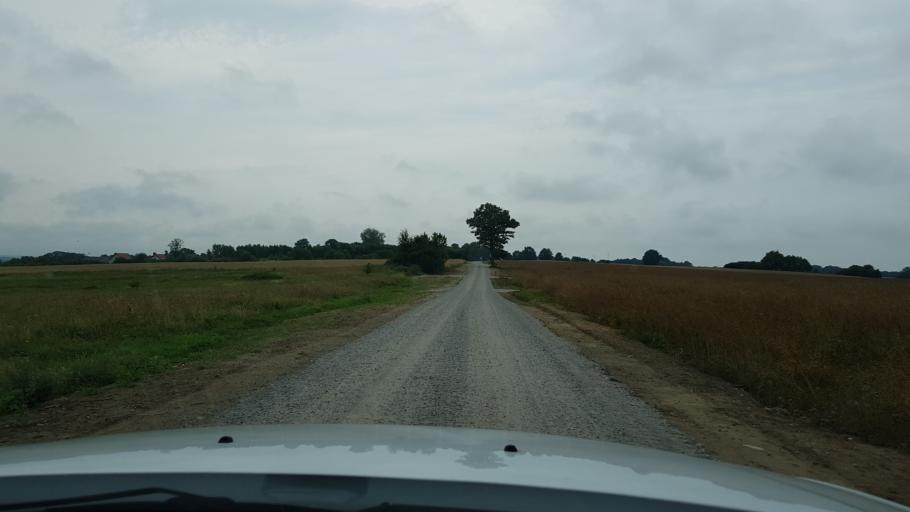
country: PL
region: West Pomeranian Voivodeship
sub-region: Powiat slawienski
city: Darlowo
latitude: 54.4623
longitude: 16.4964
